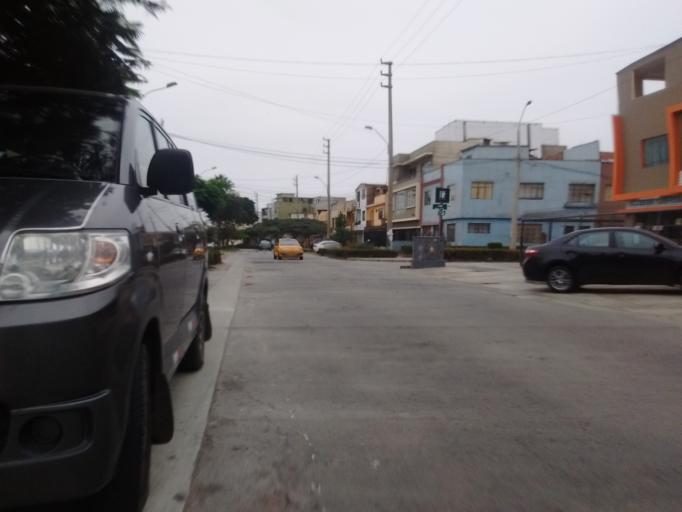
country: PE
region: Lima
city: Lima
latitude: -12.0682
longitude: -77.0566
